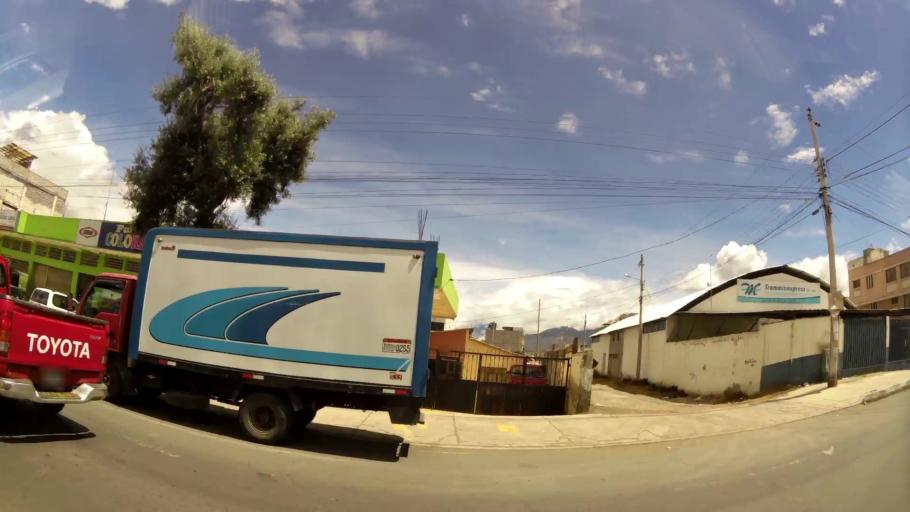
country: EC
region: Tungurahua
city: Ambato
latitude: -1.2766
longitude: -78.6300
